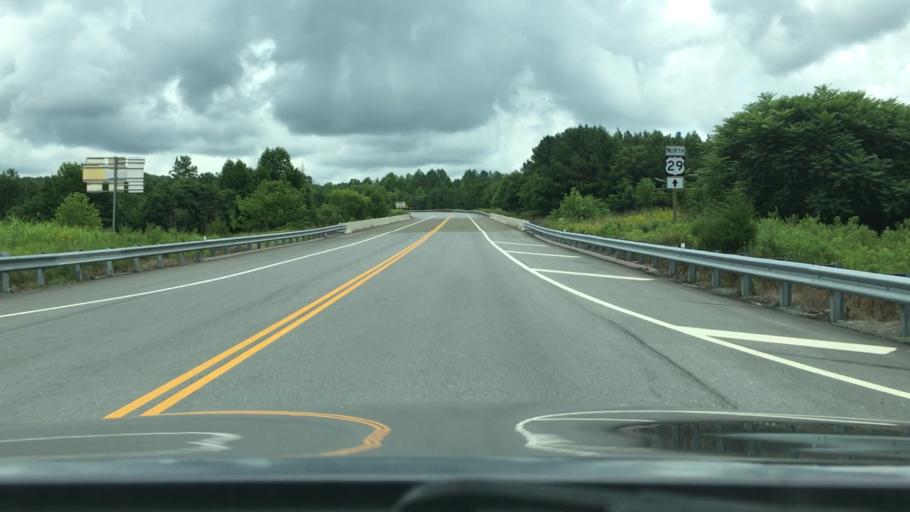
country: US
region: Virginia
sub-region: Amherst County
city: Madison Heights
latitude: 37.4083
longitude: -79.0855
